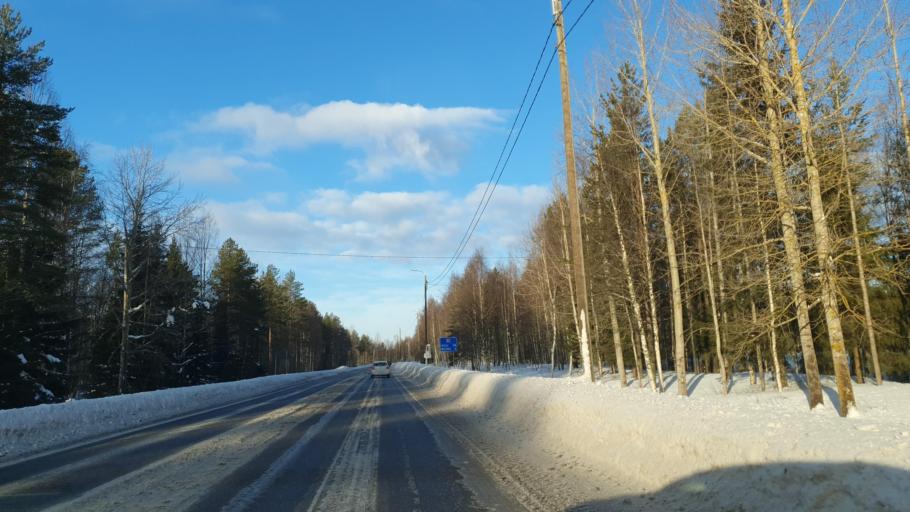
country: FI
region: Northern Ostrobothnia
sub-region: Oulu
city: Muhos
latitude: 64.7960
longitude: 26.0616
